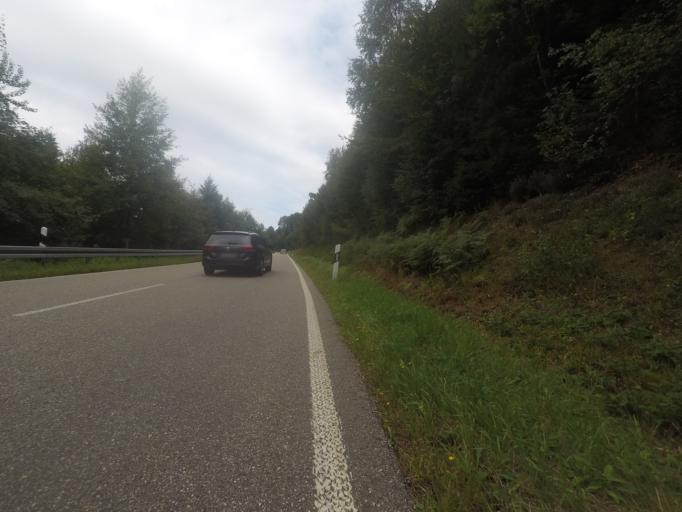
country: DE
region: Baden-Wuerttemberg
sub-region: Karlsruhe Region
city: Gaggenau
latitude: 48.8349
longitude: 8.3725
